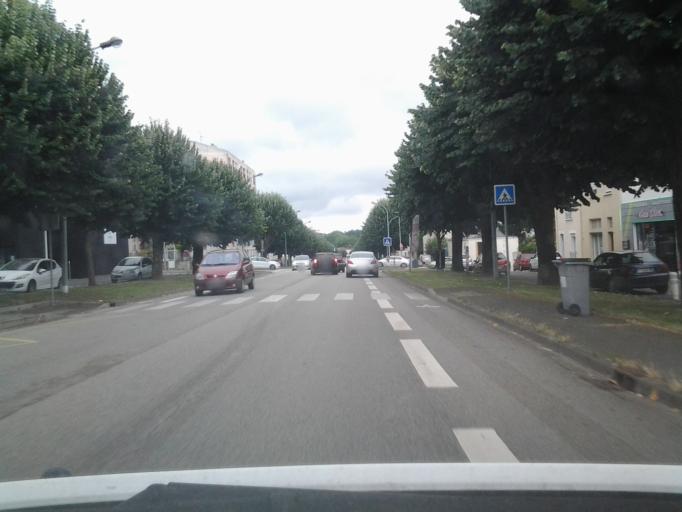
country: FR
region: Pays de la Loire
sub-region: Departement de la Vendee
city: La Roche-sur-Yon
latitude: 46.6748
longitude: -1.4233
